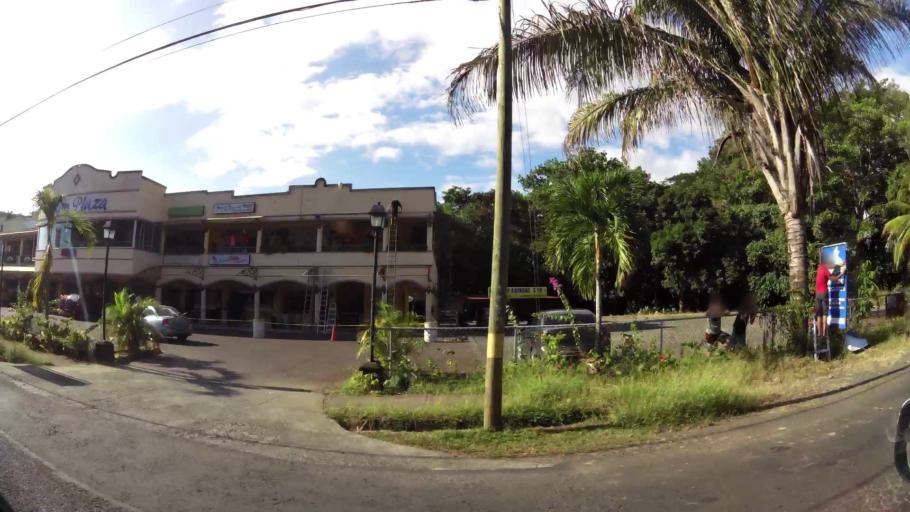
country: CR
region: Puntarenas
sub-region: Canton de Garabito
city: Jaco
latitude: 9.6537
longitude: -84.6505
